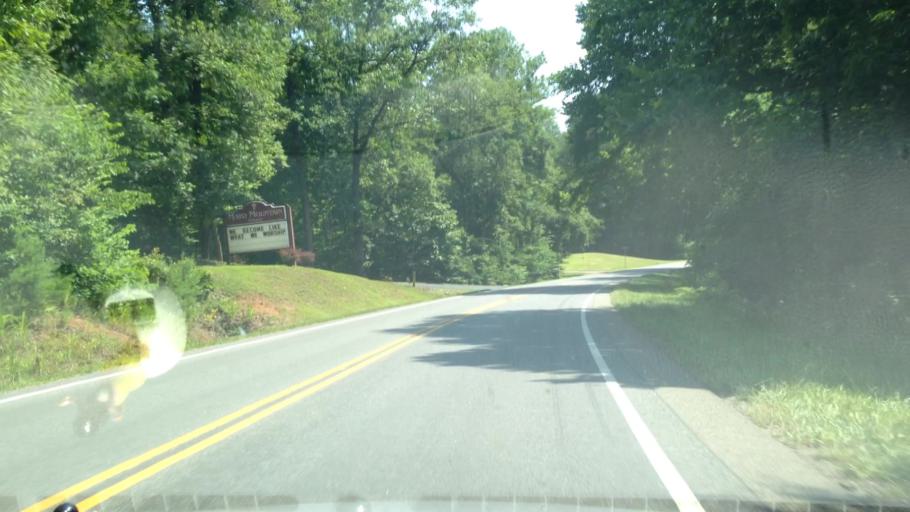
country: US
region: Virginia
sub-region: Patrick County
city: Stuart
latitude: 36.5937
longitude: -80.3156
